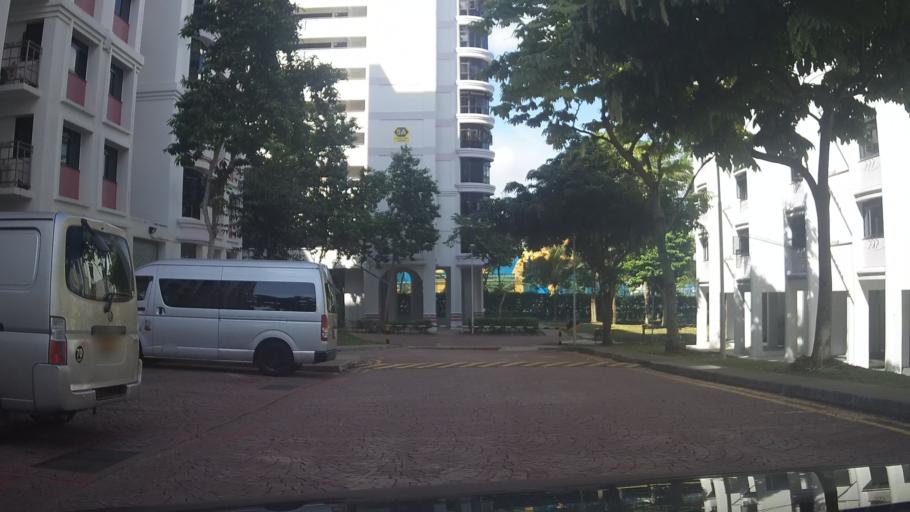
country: MY
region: Johor
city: Johor Bahru
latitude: 1.4406
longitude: 103.7758
